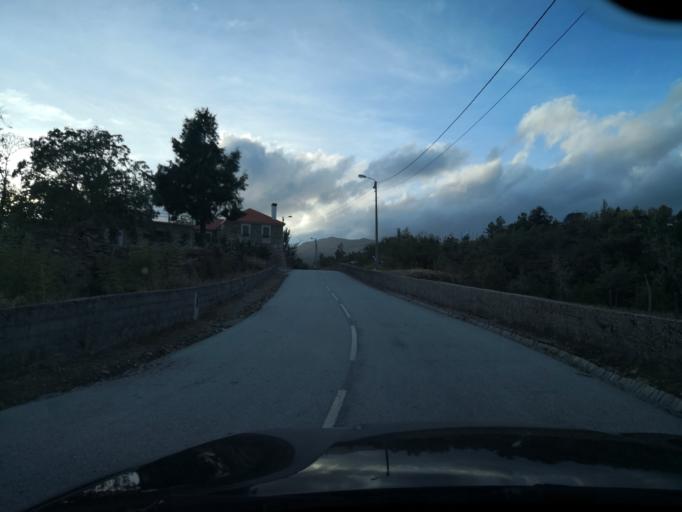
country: PT
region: Vila Real
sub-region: Santa Marta de Penaguiao
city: Santa Marta de Penaguiao
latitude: 41.2282
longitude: -7.8300
